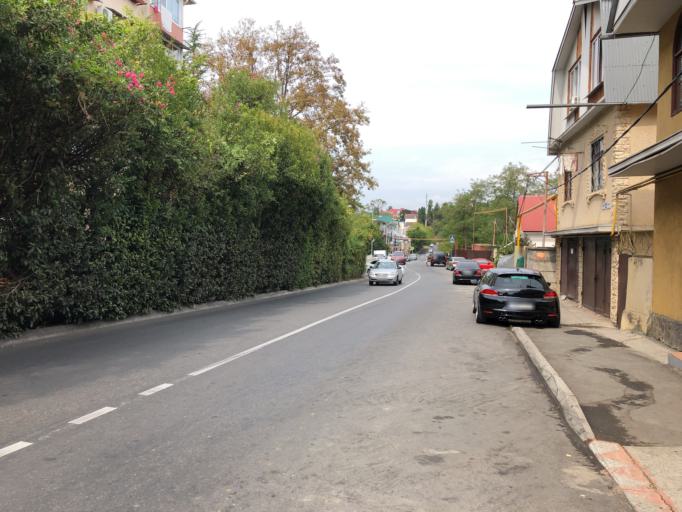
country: RU
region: Krasnodarskiy
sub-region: Sochi City
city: Sochi
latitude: 43.5931
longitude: 39.7417
